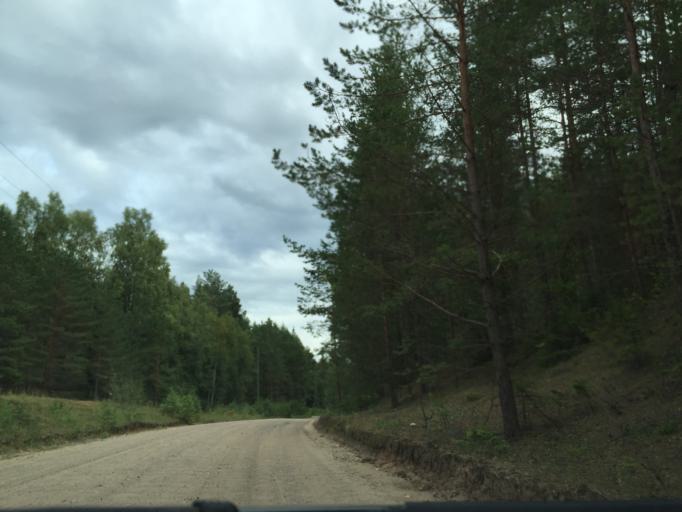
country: LV
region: Saulkrastu
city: Saulkrasti
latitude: 57.1858
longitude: 24.3695
